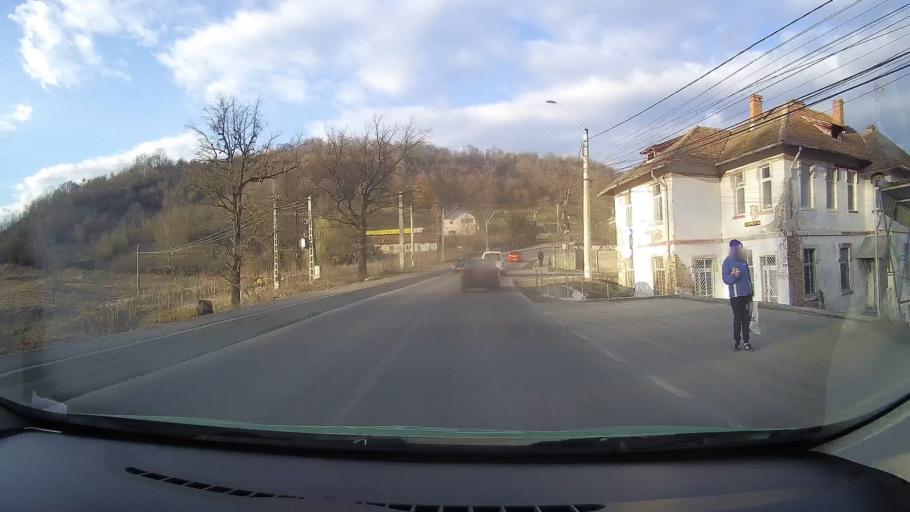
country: RO
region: Dambovita
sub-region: Municipiul Moreni
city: Moreni
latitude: 44.9772
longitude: 25.6200
